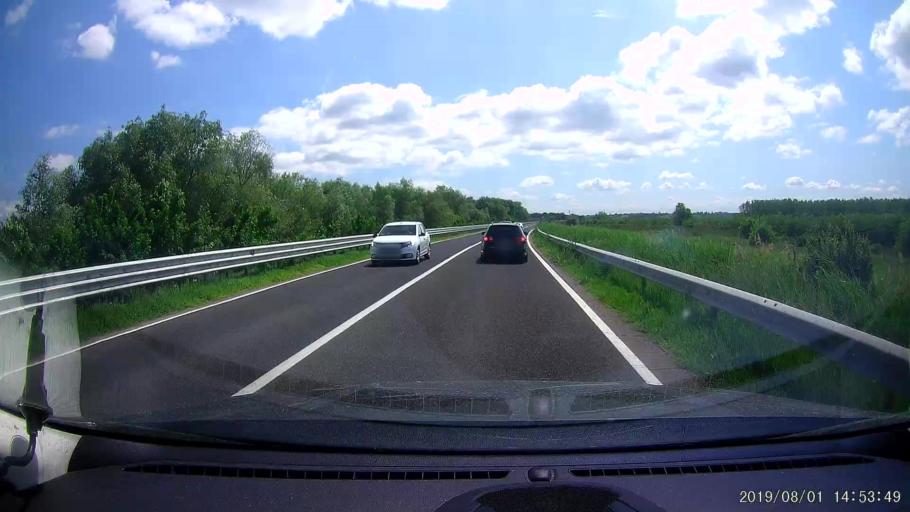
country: RO
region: Braila
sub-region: Municipiul Braila
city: Braila
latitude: 45.3282
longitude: 27.9986
